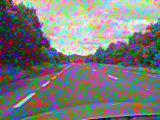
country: IE
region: Ulster
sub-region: County Donegal
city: Donegal
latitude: 54.6888
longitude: -8.0154
